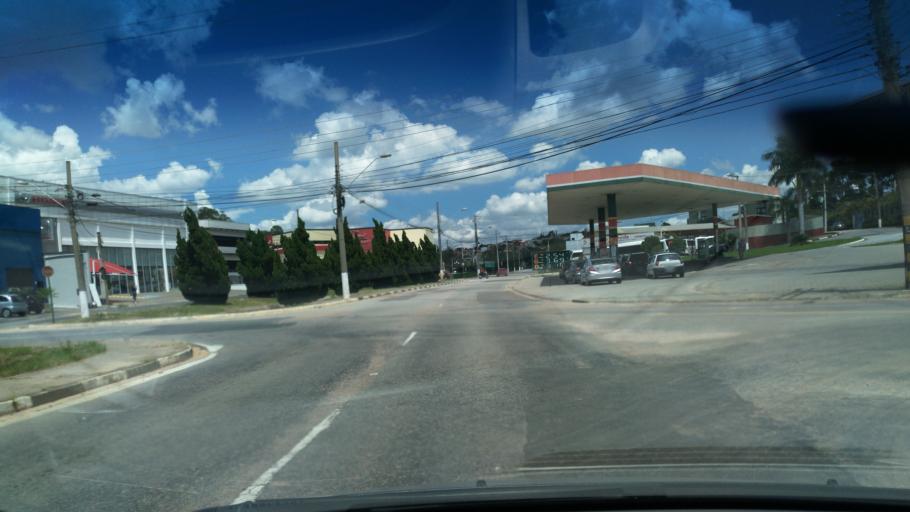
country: BR
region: Sao Paulo
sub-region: Vinhedo
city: Vinhedo
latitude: -23.0075
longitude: -46.9877
